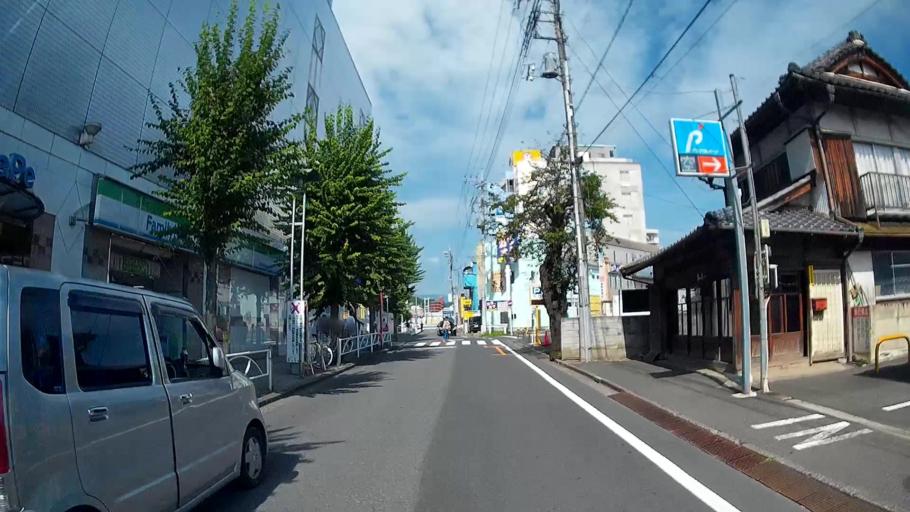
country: JP
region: Saitama
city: Hanno
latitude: 35.8514
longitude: 139.3193
